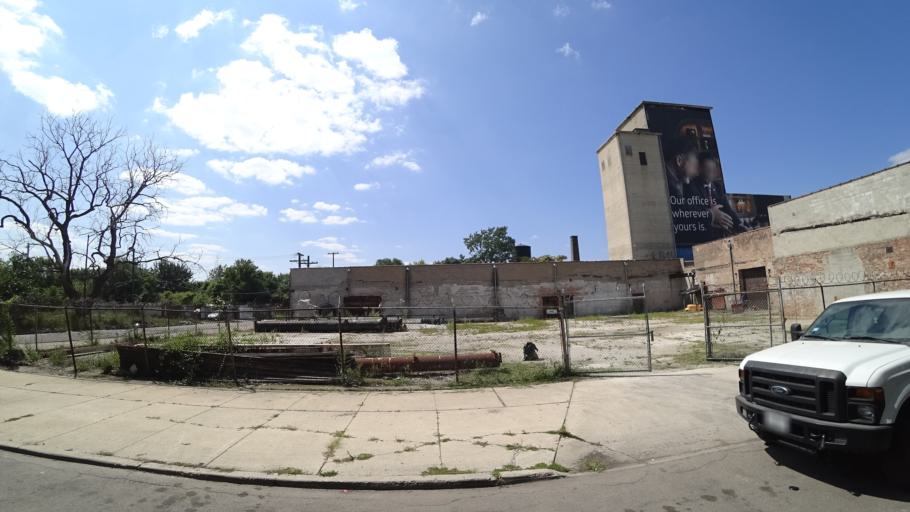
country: US
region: Illinois
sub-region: Cook County
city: Cicero
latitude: 41.8708
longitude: -87.7390
